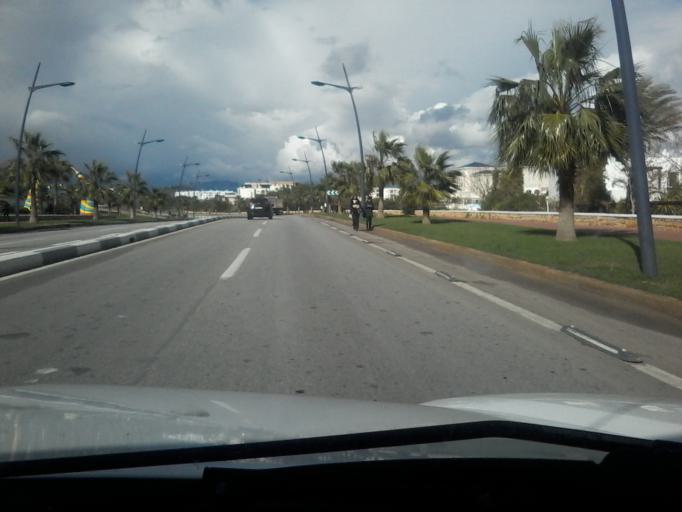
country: MA
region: Tanger-Tetouan
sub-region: Tetouan
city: Martil
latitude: 35.7426
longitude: -5.3440
